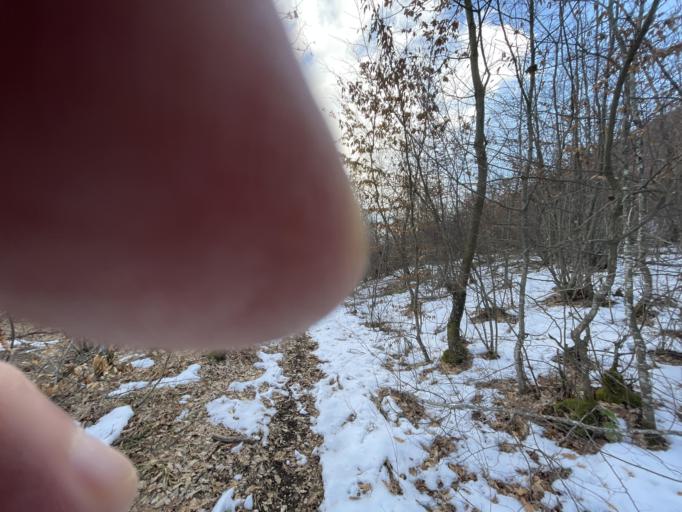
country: XK
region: Gjakova
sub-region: Komuna e Decanit
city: Strellc i Eperm
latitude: 42.5993
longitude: 20.2839
